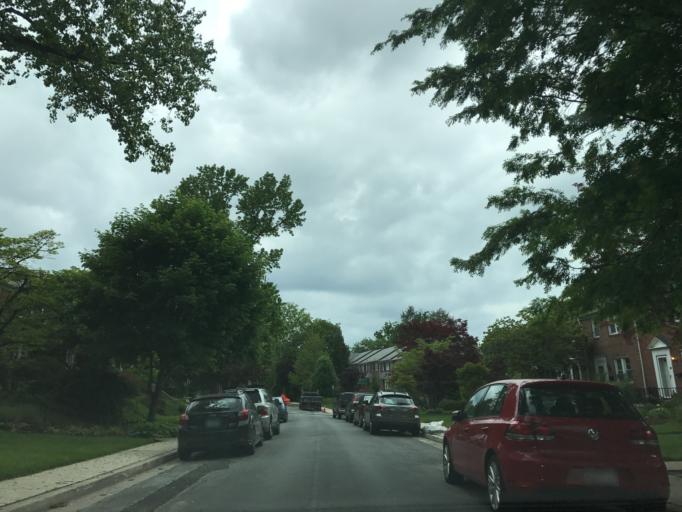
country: US
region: Maryland
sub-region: Baltimore County
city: Towson
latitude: 39.3781
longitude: -76.6163
